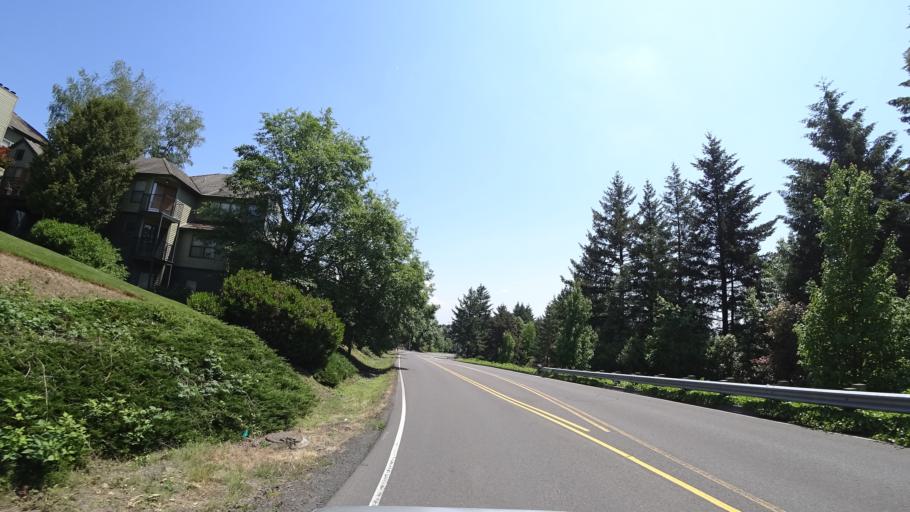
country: US
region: Oregon
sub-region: Washington County
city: Metzger
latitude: 45.4318
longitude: -122.7192
